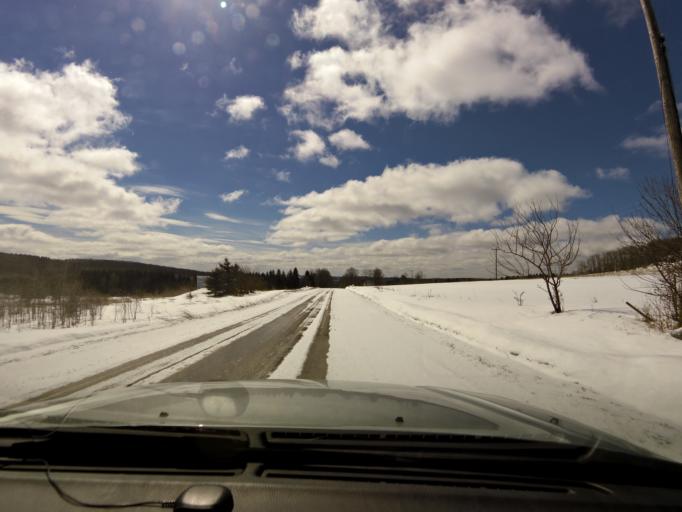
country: US
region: New York
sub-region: Cattaraugus County
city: Franklinville
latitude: 42.3454
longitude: -78.3876
